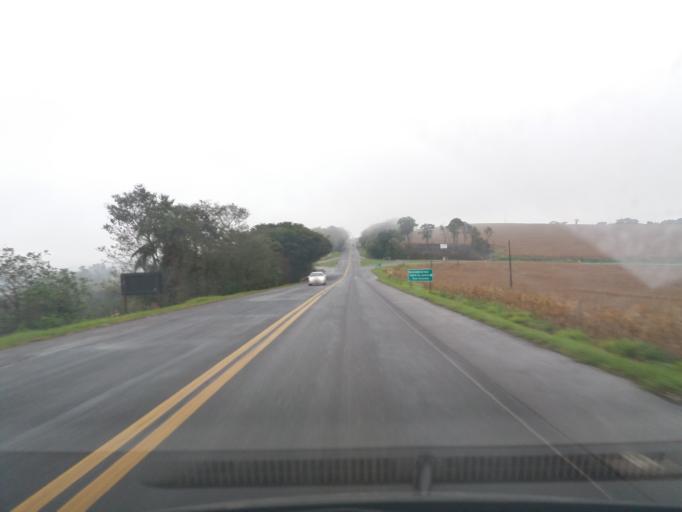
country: BR
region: Parana
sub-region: Ampere
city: Ampere
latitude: -25.8860
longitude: -53.4692
